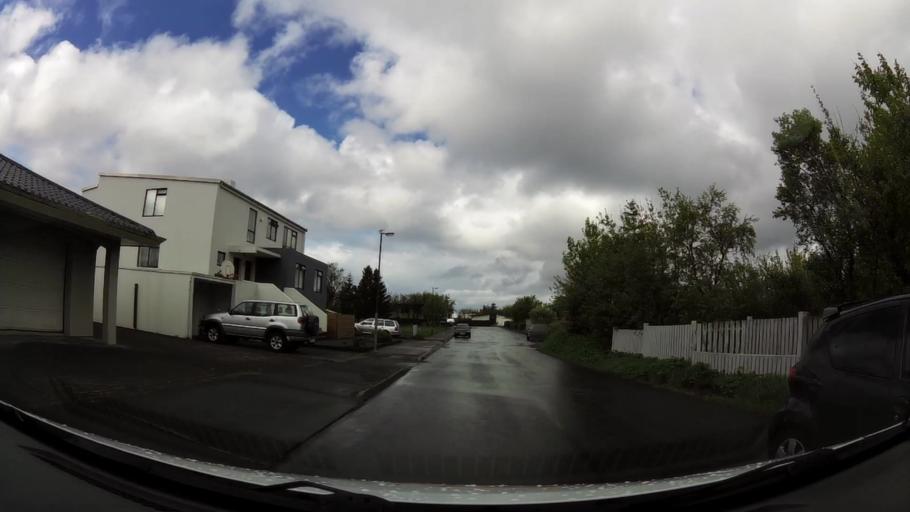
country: IS
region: Capital Region
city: Kopavogur
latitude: 64.1275
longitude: -21.9495
